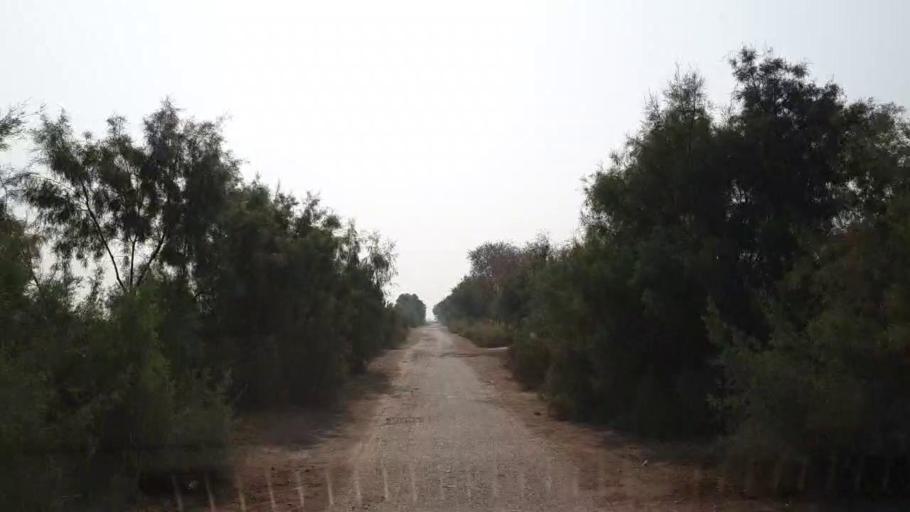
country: PK
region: Sindh
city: Bhan
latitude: 26.4670
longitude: 67.7391
